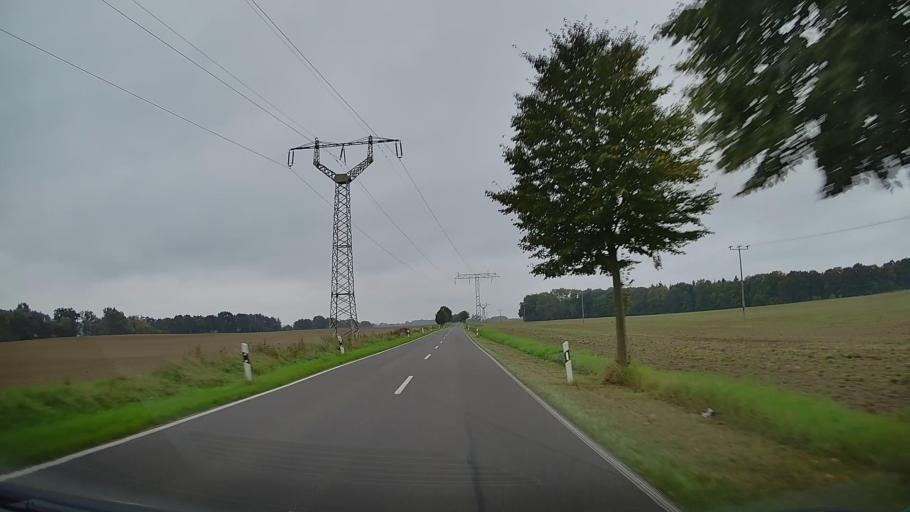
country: DE
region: Mecklenburg-Vorpommern
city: Guestrow
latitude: 53.8046
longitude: 12.1077
